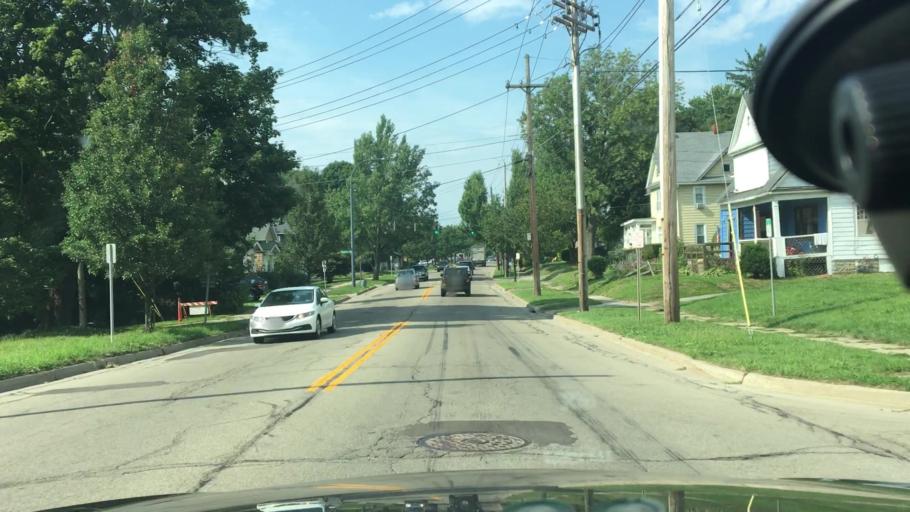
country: US
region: New York
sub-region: Chautauqua County
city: Jamestown
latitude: 42.1071
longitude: -79.2413
